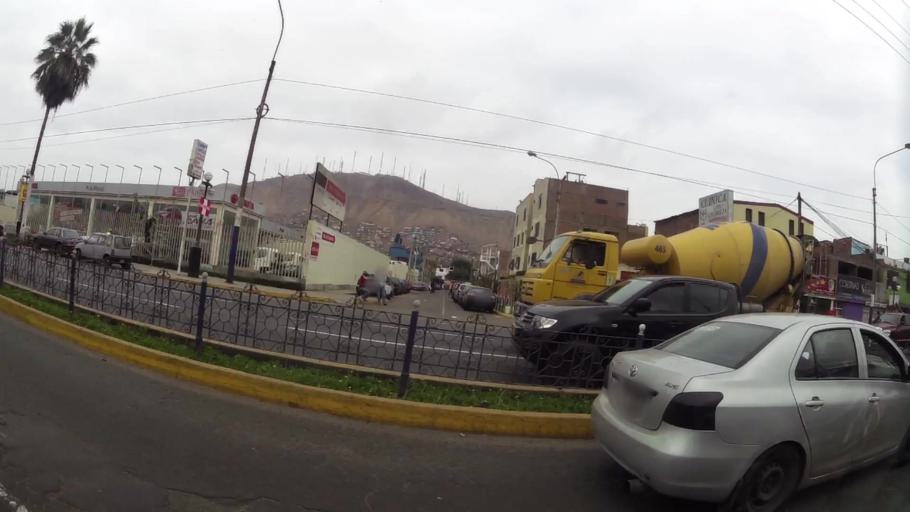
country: PE
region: Lima
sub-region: Lima
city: Surco
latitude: -12.1740
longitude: -77.0203
